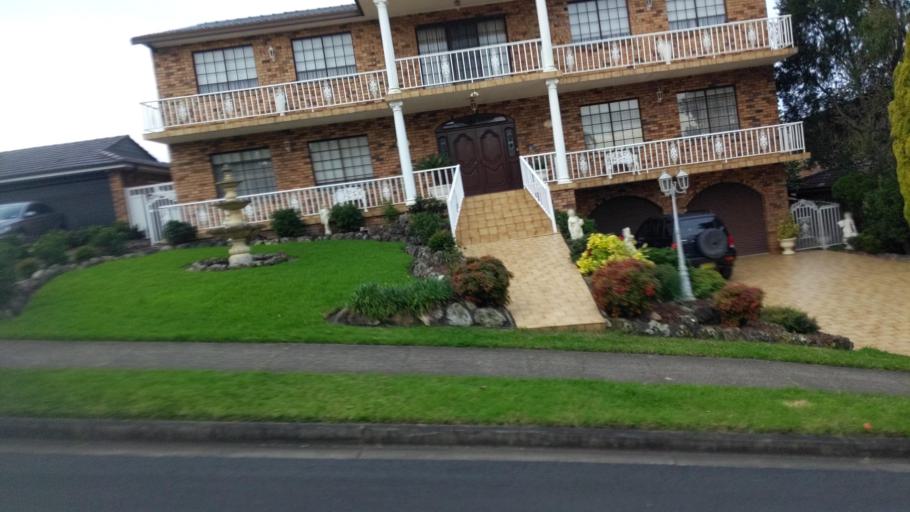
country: AU
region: New South Wales
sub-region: The Hills Shire
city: Baulkham Hills
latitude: -33.7439
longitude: 150.9677
